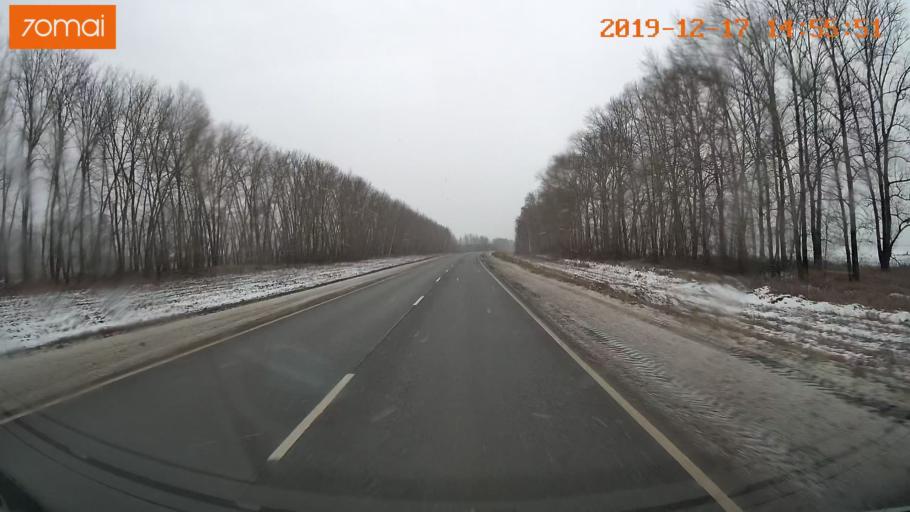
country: RU
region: Rjazan
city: Zakharovo
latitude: 54.3473
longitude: 39.2598
